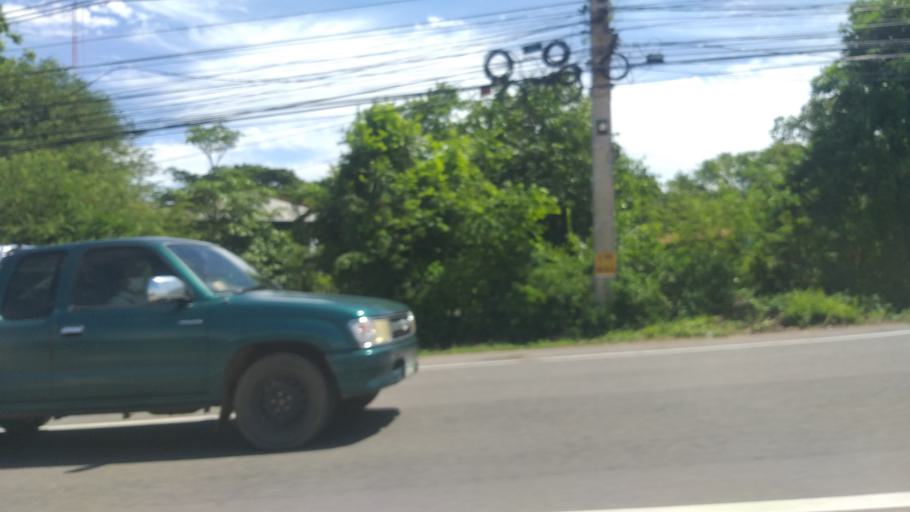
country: TH
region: Khon Kaen
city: Ban Fang
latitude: 16.4485
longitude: 102.6468
